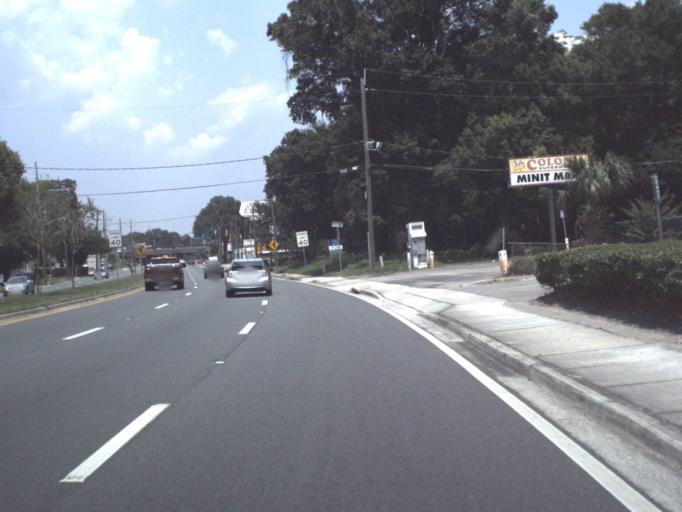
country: US
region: Florida
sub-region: Duval County
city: Jacksonville
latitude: 30.3065
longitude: -81.6235
